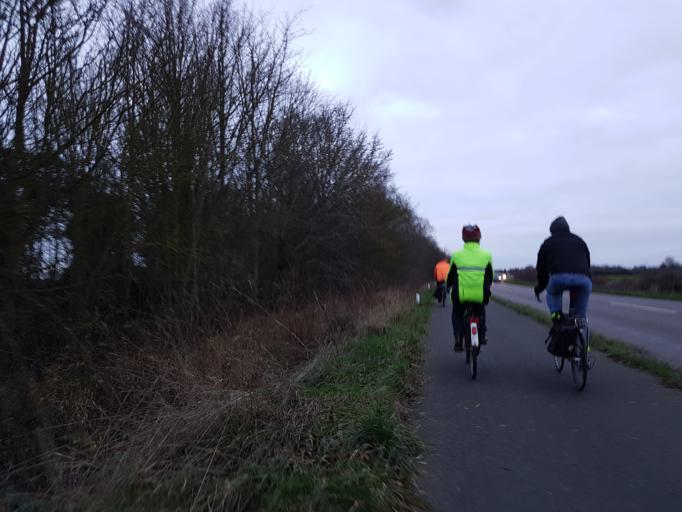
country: GB
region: England
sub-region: Cambridgeshire
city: Bottisham
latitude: 52.2305
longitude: 0.2350
